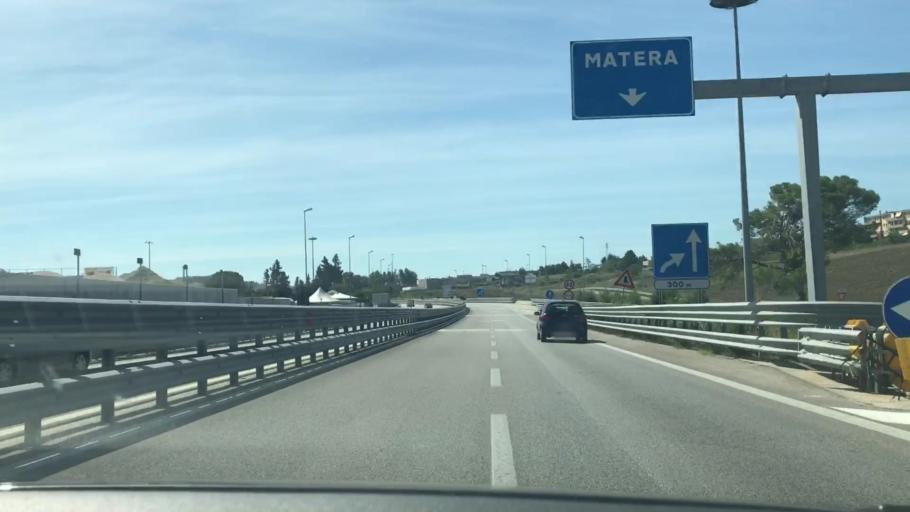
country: IT
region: Basilicate
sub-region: Provincia di Matera
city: Matera
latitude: 40.6908
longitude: 16.5909
